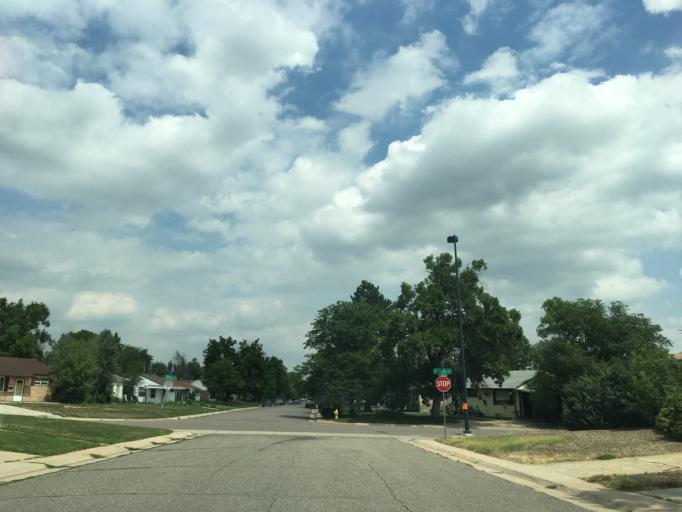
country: US
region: Colorado
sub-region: Arapahoe County
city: Sheridan
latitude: 39.6672
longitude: -105.0271
